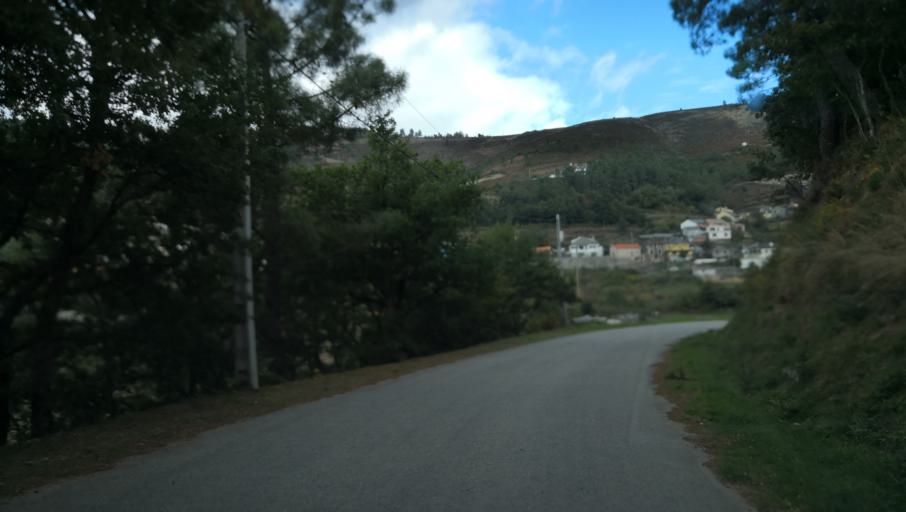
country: PT
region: Vila Real
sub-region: Vila Real
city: Vila Real
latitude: 41.3634
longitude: -7.8430
